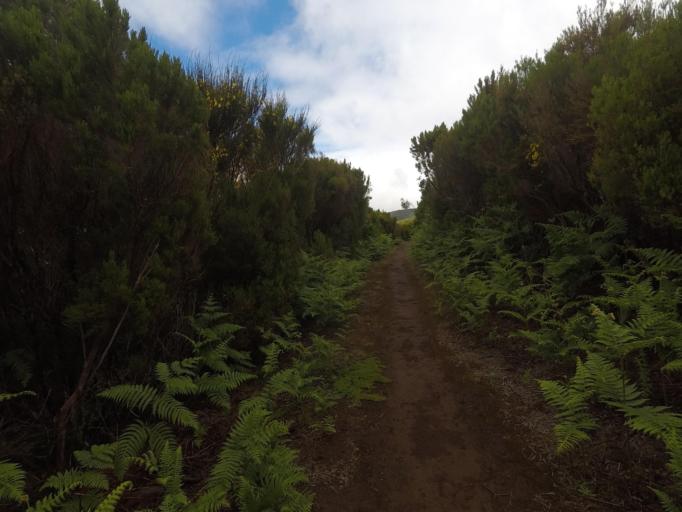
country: PT
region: Madeira
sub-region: Calheta
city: Arco da Calheta
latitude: 32.7755
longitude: -17.1335
